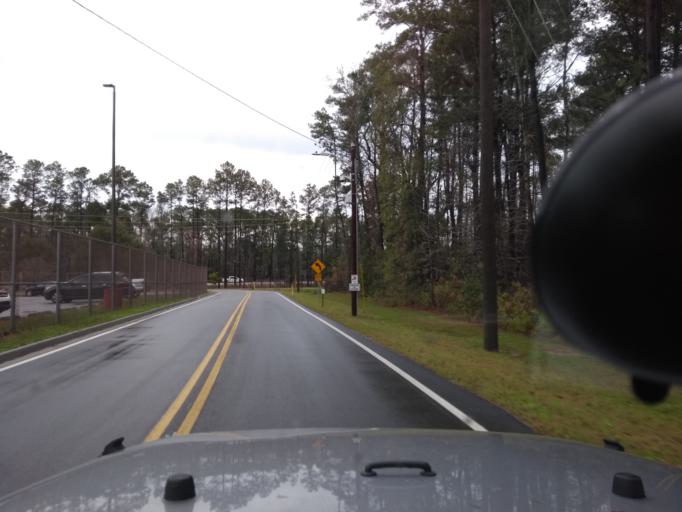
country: US
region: Georgia
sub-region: Chatham County
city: Garden City
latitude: 32.0678
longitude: -81.1656
